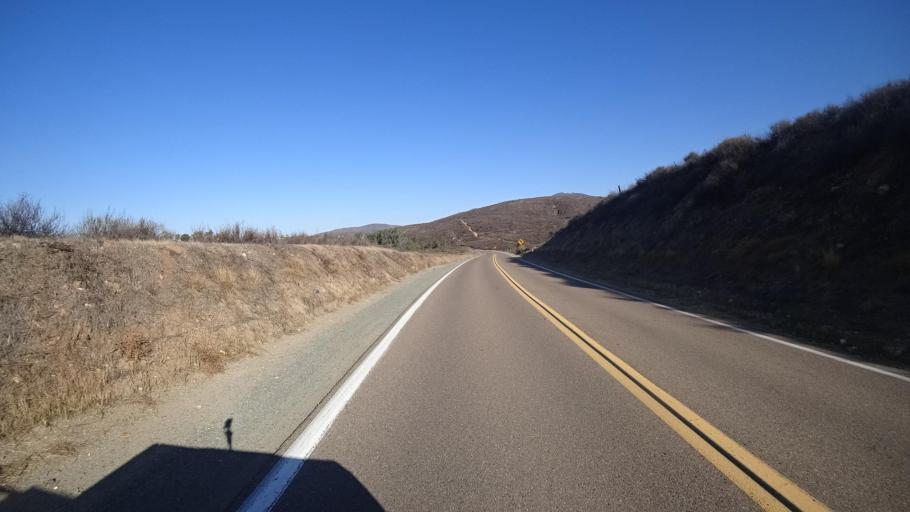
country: US
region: California
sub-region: San Diego County
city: Jamul
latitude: 32.6456
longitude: -116.9271
